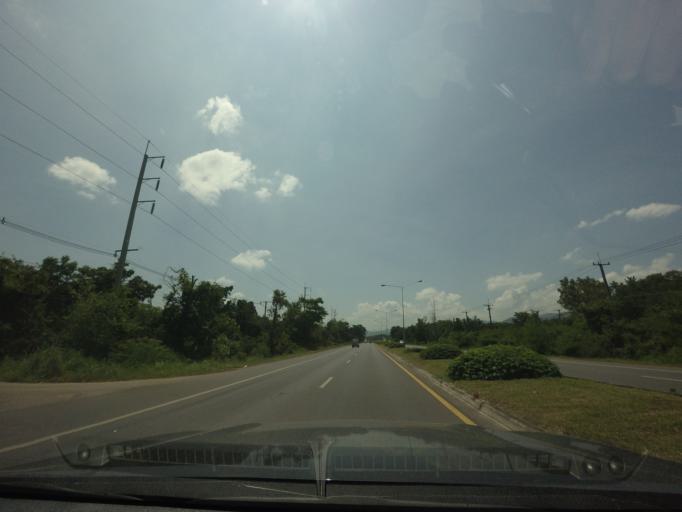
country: TH
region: Phetchabun
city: Lom Sak
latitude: 16.6931
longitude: 101.1685
